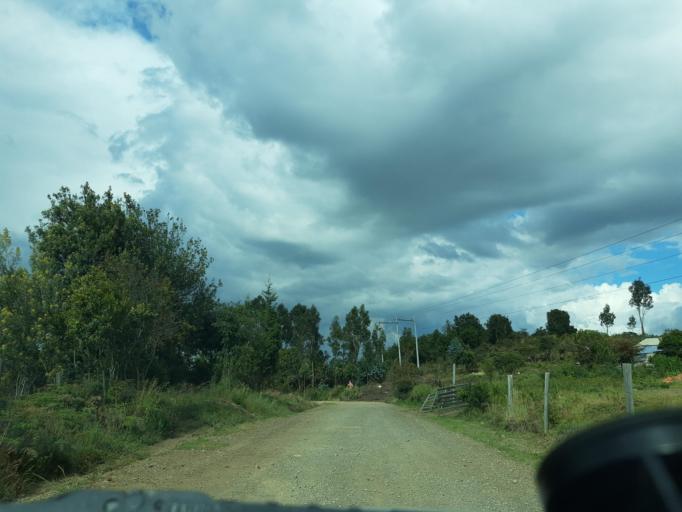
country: CO
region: Boyaca
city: Raquira
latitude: 5.5229
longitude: -73.6644
